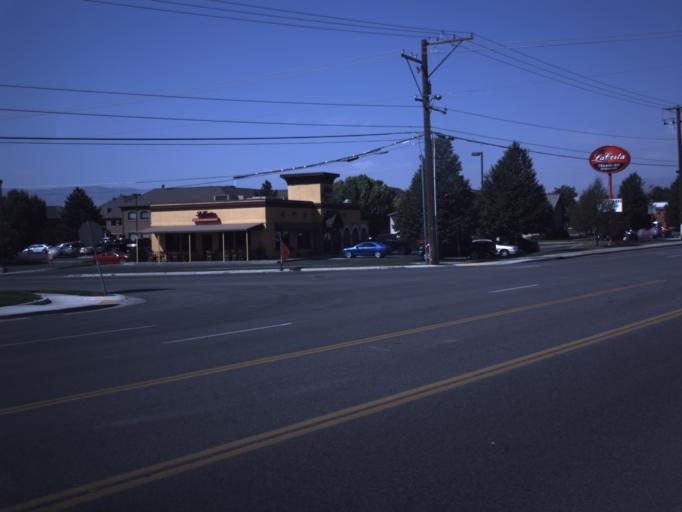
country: US
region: Utah
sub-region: Utah County
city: American Fork
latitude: 40.3713
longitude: -111.7740
